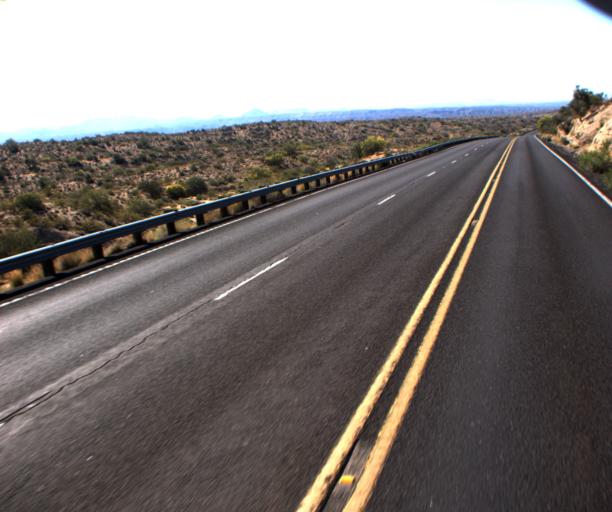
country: US
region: Arizona
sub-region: Mohave County
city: Kingman
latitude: 34.9341
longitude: -113.6614
